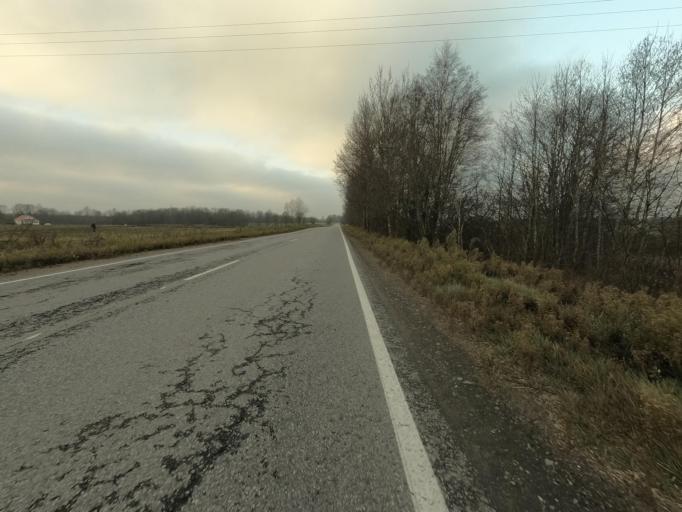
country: RU
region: Leningrad
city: Mga
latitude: 59.7663
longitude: 31.0198
